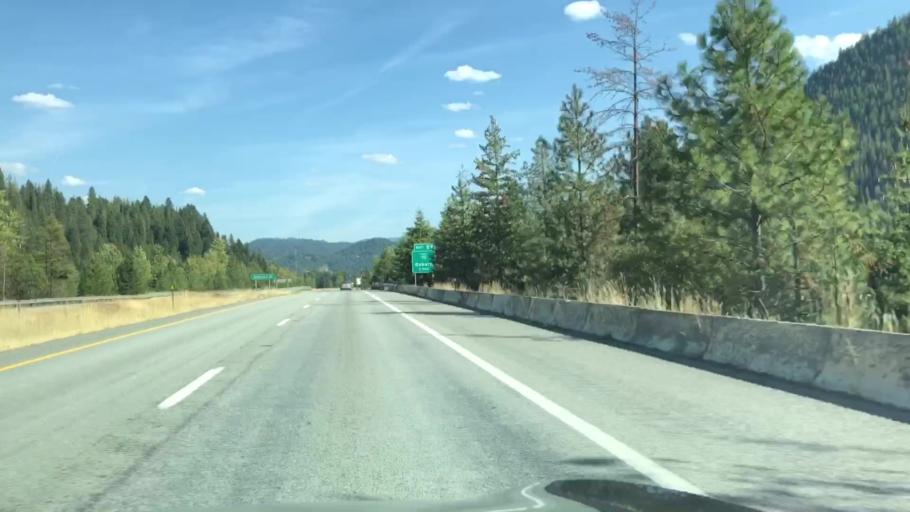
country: US
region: Idaho
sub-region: Shoshone County
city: Osburn
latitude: 47.5136
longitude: -116.0255
